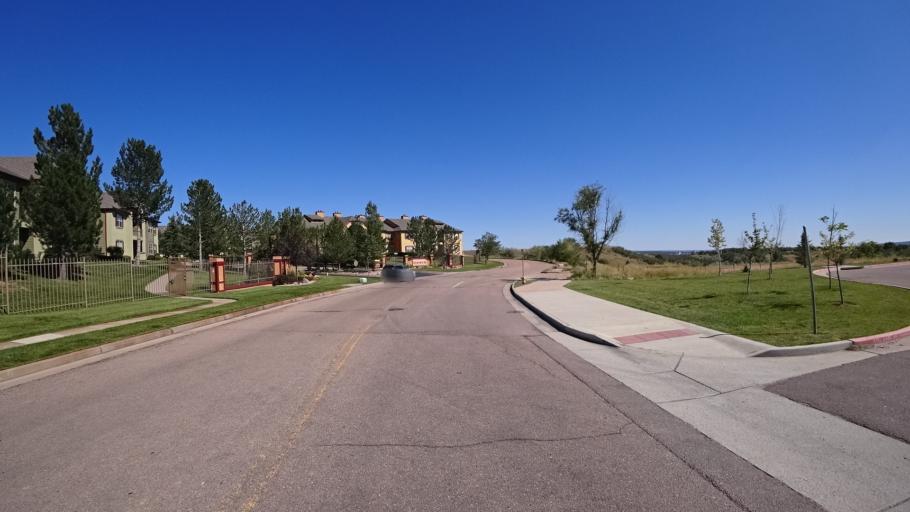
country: US
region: Colorado
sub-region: El Paso County
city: Colorado Springs
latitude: 38.8723
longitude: -104.8549
